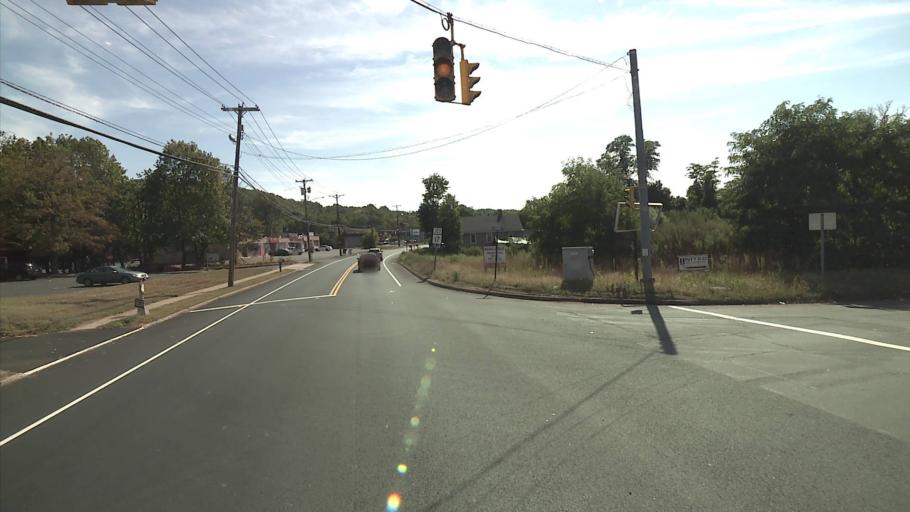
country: US
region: Connecticut
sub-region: New Haven County
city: North Haven
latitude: 41.3423
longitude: -72.8637
